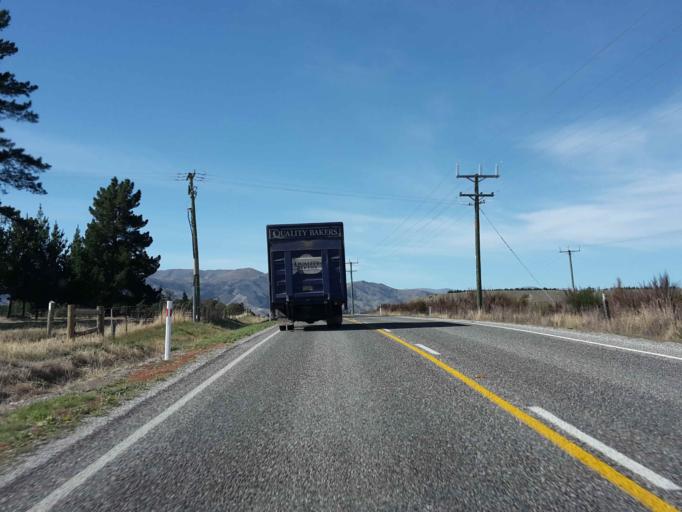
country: NZ
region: Otago
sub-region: Queenstown-Lakes District
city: Wanaka
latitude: -44.7193
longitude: 169.2234
